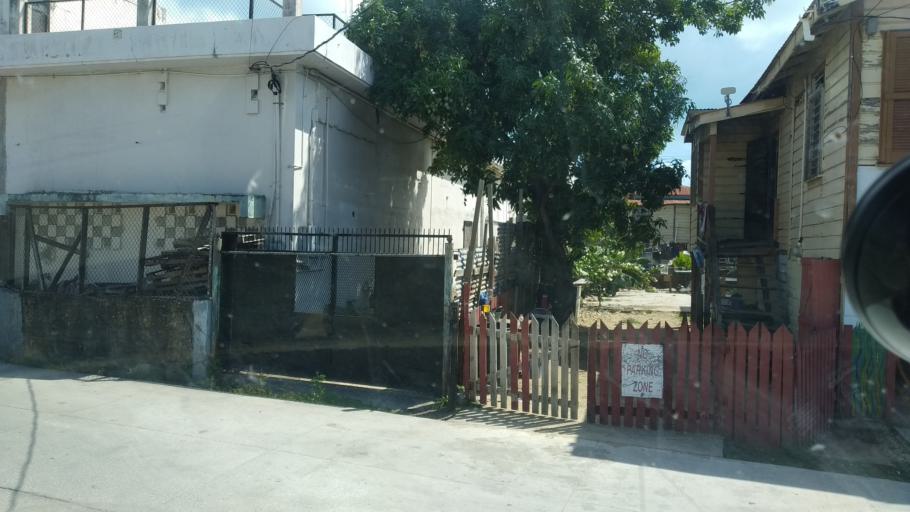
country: BZ
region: Belize
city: Belize City
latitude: 17.5024
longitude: -88.1904
